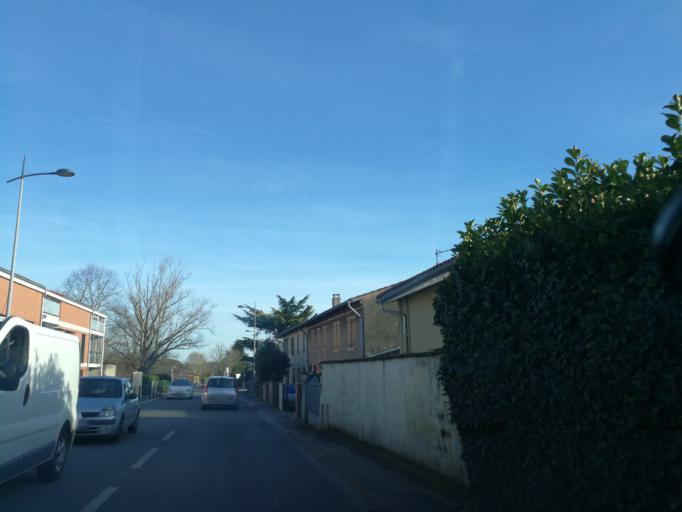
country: FR
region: Midi-Pyrenees
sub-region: Departement de la Haute-Garonne
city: Saint-Jean
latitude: 43.6518
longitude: 1.4982
